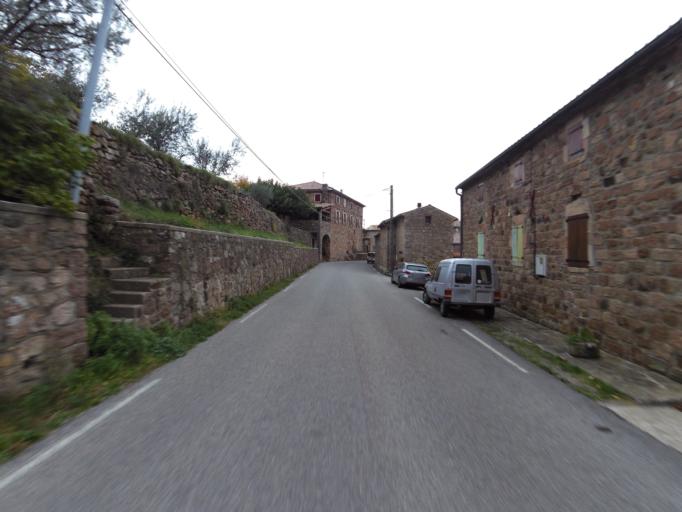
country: FR
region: Rhone-Alpes
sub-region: Departement de l'Ardeche
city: Lablachere
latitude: 44.4835
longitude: 4.1629
